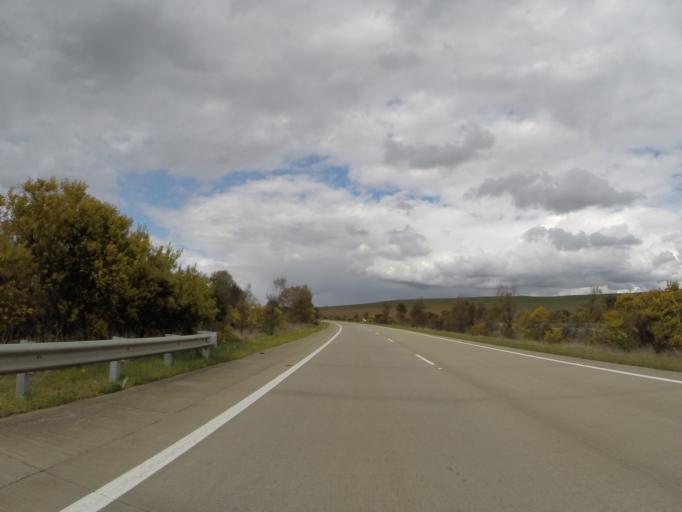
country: AU
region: New South Wales
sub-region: Goulburn Mulwaree
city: Goulburn
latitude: -34.8074
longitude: 149.5198
